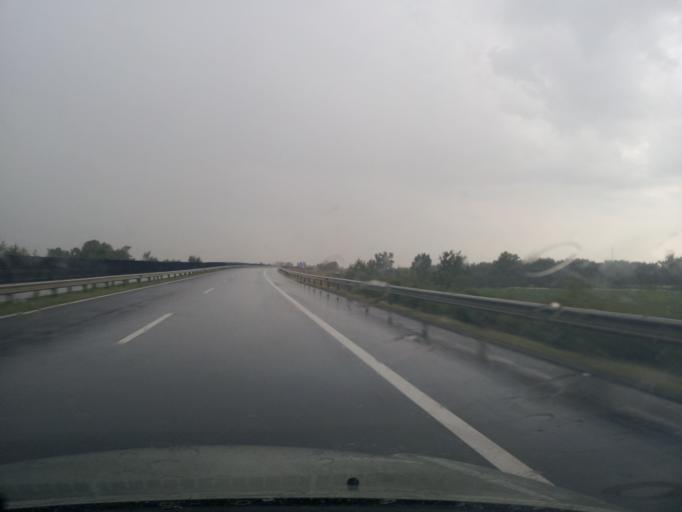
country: HU
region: Borsod-Abauj-Zemplen
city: Felsozsolca
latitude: 48.0914
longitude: 20.8500
